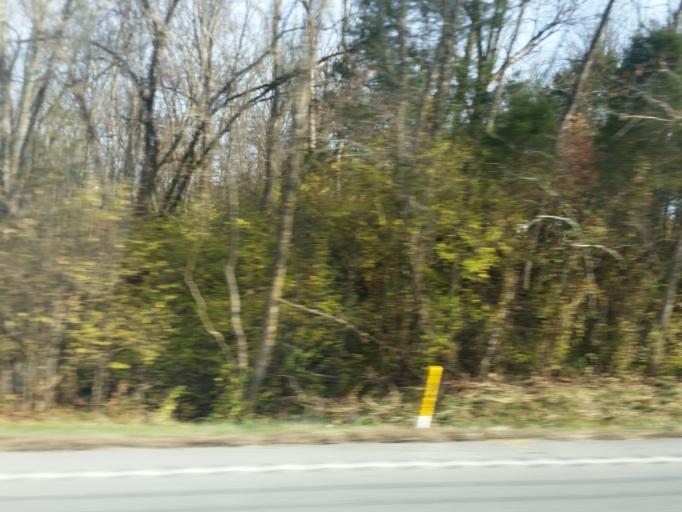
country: US
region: Kentucky
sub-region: Pendleton County
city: Falmouth
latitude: 38.7314
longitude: -84.3719
